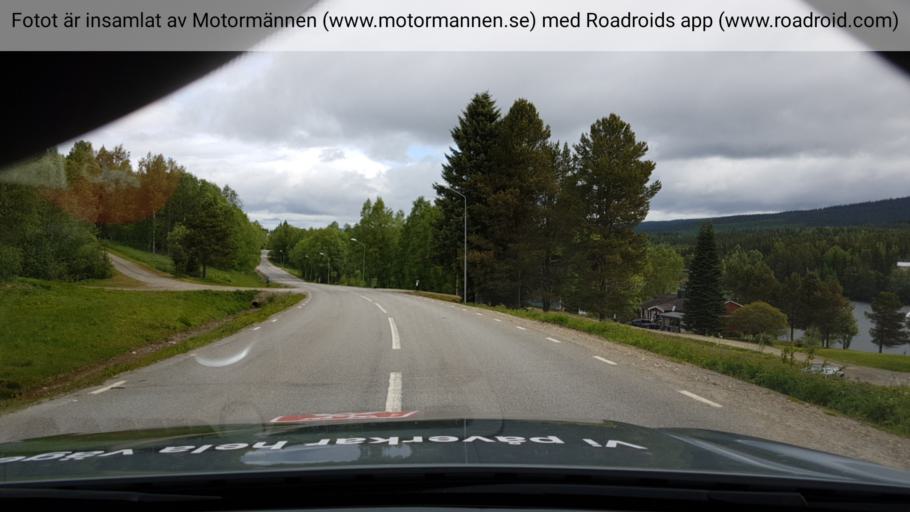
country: NO
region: Nord-Trondelag
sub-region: Lierne
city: Sandvika
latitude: 64.4936
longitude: 14.1399
